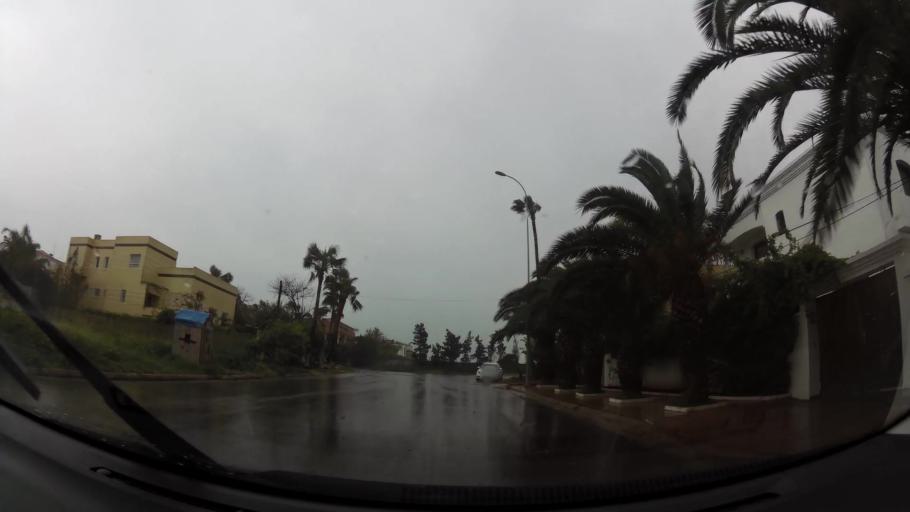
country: MA
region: Grand Casablanca
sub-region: Casablanca
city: Casablanca
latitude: 33.5845
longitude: -7.6766
